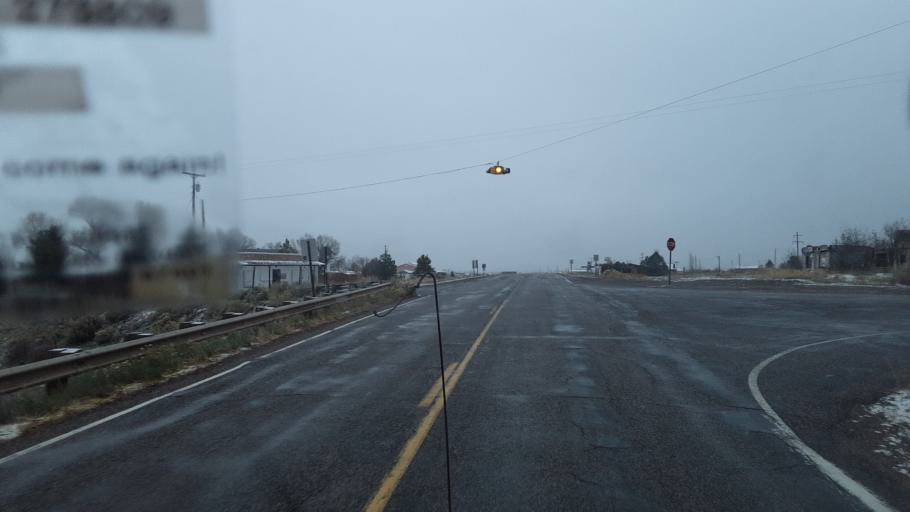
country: US
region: New Mexico
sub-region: Rio Arriba County
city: Tierra Amarilla
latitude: 36.7007
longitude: -106.5581
